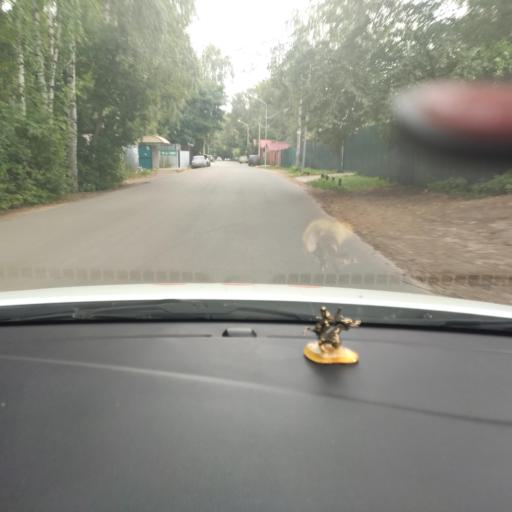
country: RU
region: Tatarstan
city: Verkhniy Uslon
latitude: 55.5992
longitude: 49.0224
